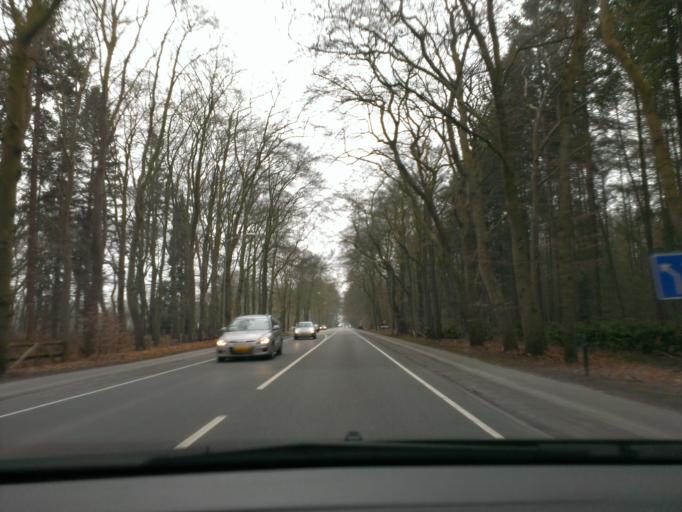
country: NL
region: Gelderland
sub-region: Gemeente Hattem
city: Hattem
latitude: 52.4503
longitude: 6.0691
